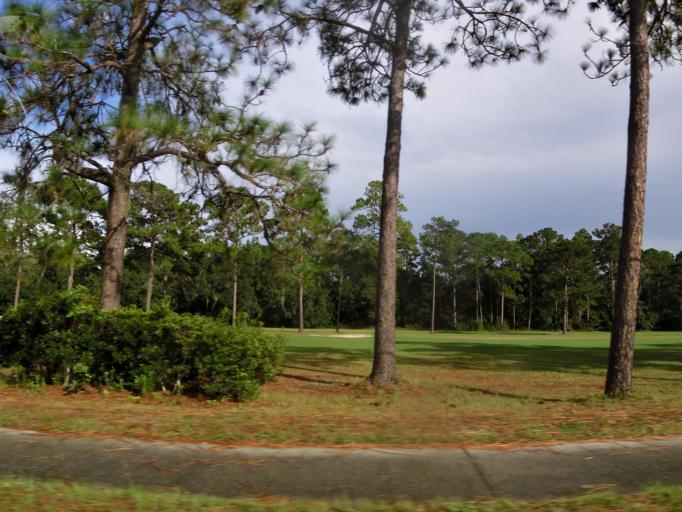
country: US
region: Georgia
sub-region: Liberty County
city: Walthourville
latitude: 31.8036
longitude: -81.6047
